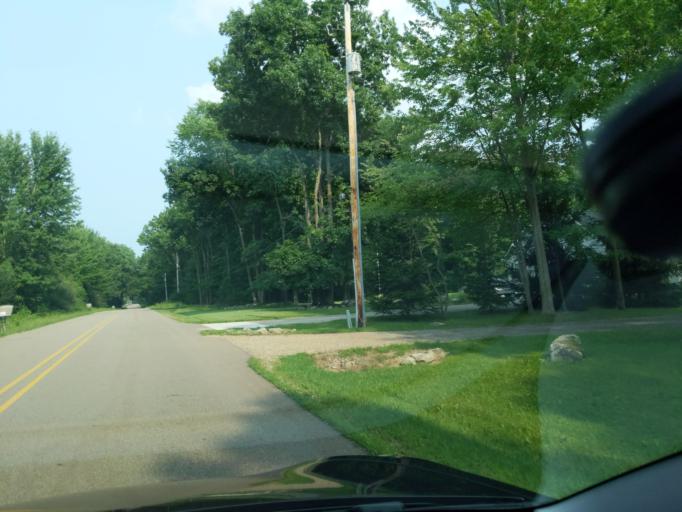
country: US
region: Michigan
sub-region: Jackson County
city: Spring Arbor
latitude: 42.2621
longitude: -84.4957
